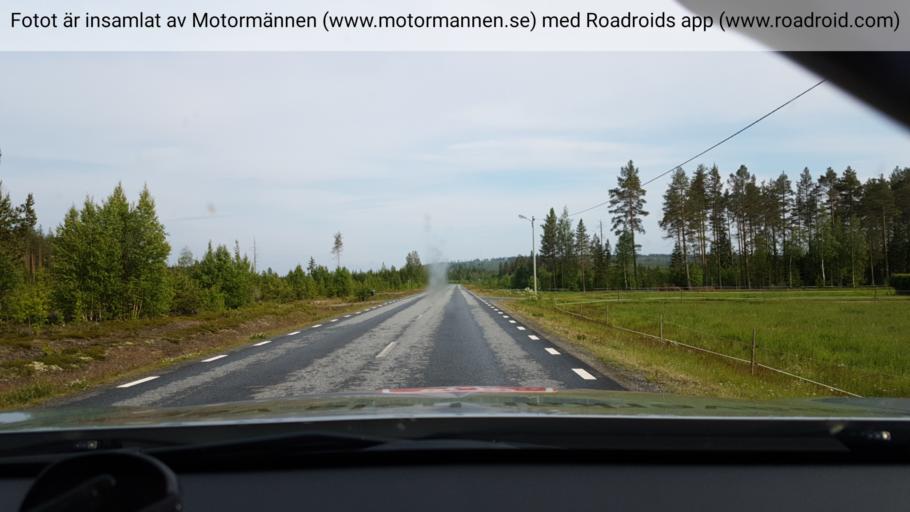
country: SE
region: Vaesterbotten
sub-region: Bjurholms Kommun
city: Bjurholm
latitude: 64.2997
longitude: 19.1746
